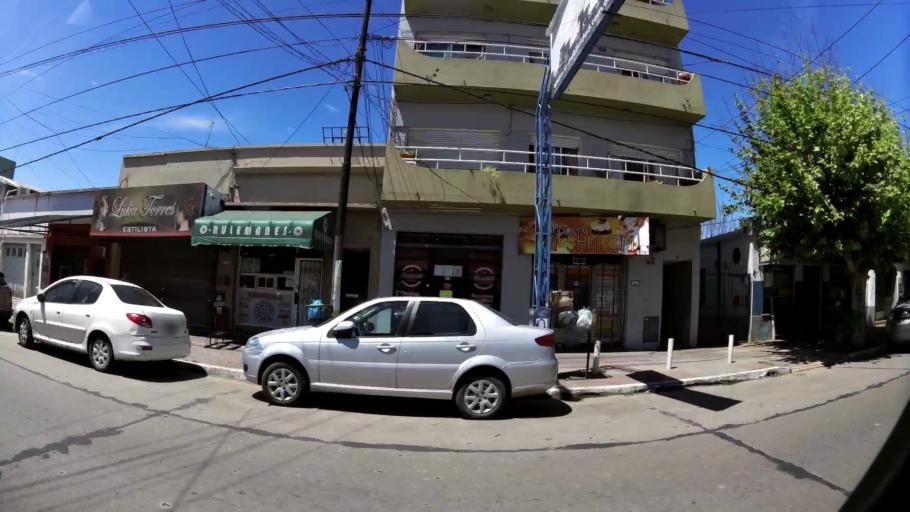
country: AR
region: Buenos Aires
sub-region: Partido de Quilmes
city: Quilmes
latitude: -34.7332
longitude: -58.2713
